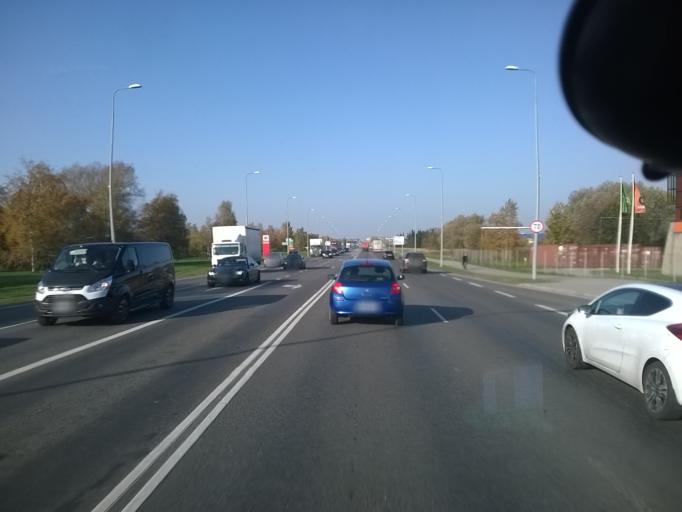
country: EE
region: Harju
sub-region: Tallinna linn
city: Tallinn
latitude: 59.4082
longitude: 24.8062
